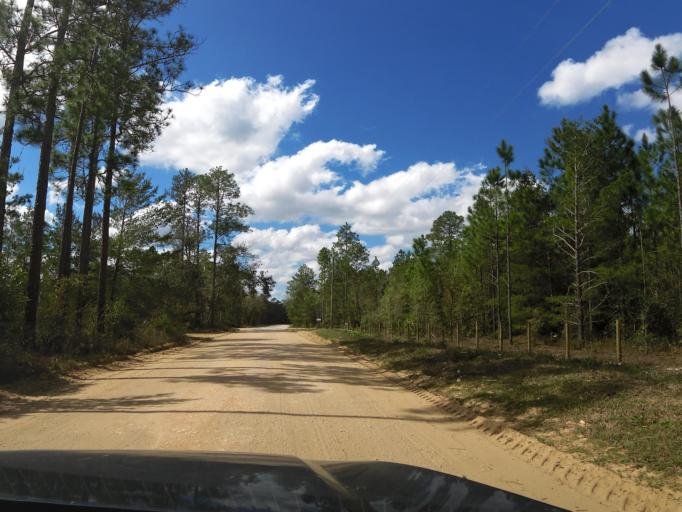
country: US
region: Florida
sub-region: Clay County
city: Keystone Heights
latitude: 29.8108
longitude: -81.8453
